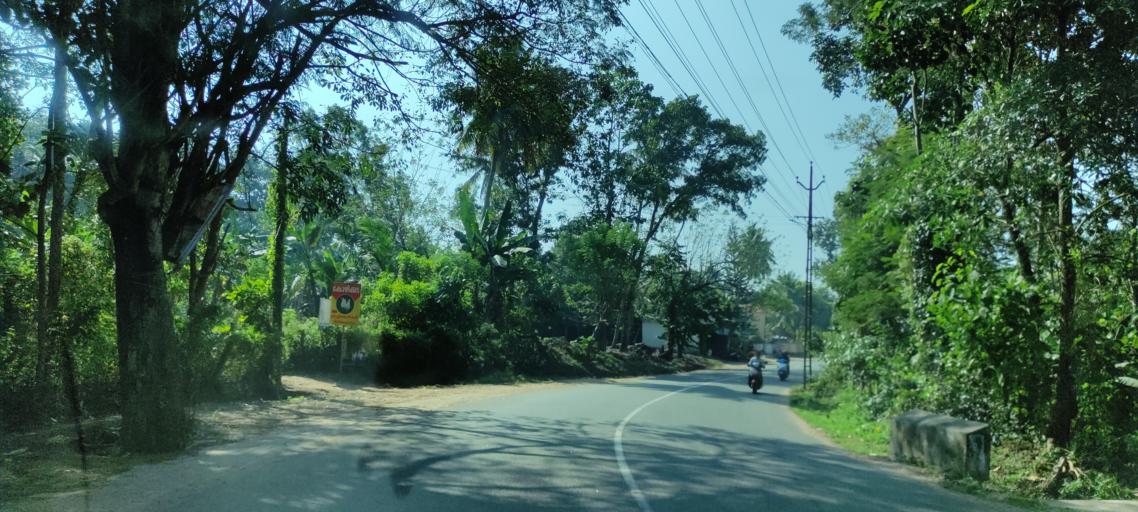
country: IN
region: Kerala
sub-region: Pattanamtitta
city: Adur
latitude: 9.1007
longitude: 76.6889
